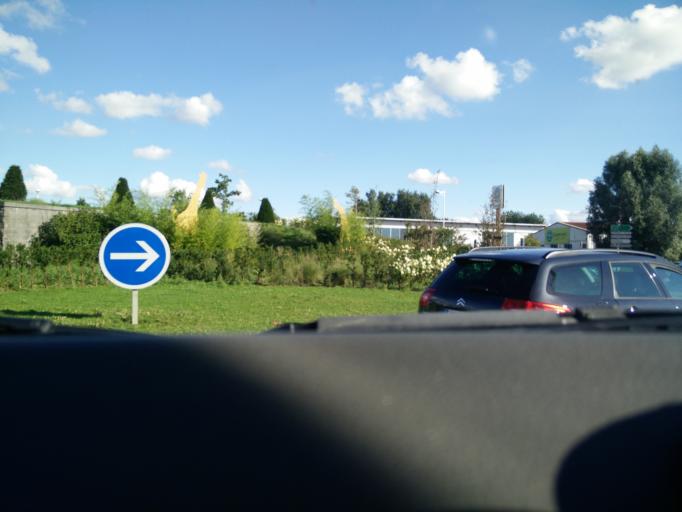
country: FR
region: Nord-Pas-de-Calais
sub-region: Departement du Nord
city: Feignies
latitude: 50.2802
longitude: 3.9228
